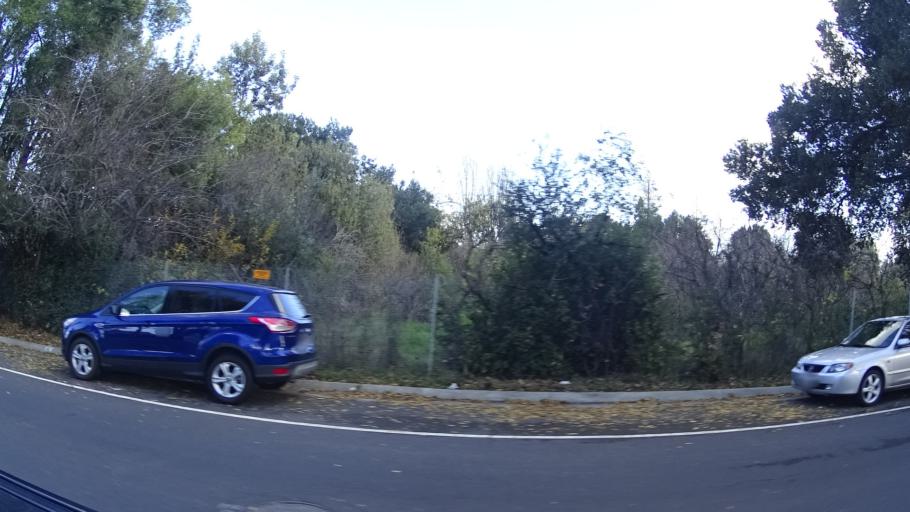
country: US
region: California
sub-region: Santa Clara County
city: Sunnyvale
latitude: 37.3836
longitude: -122.0344
